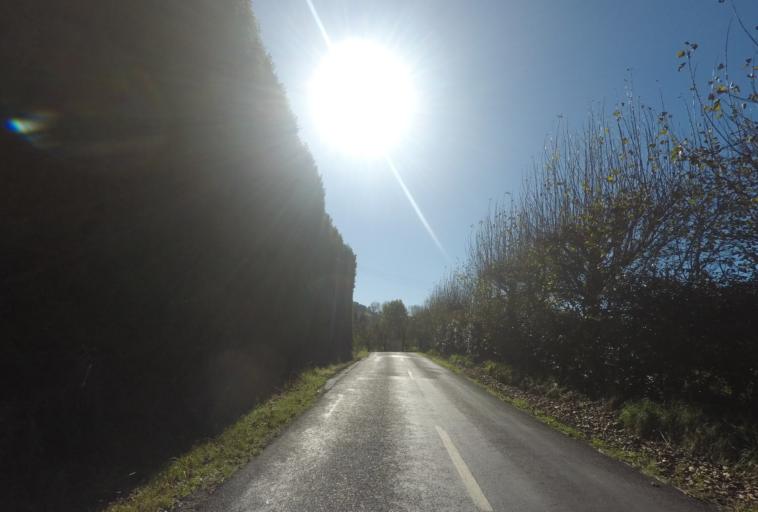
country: NZ
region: Bay of Plenty
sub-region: Western Bay of Plenty District
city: Waihi Beach
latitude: -37.4020
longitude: 175.9058
